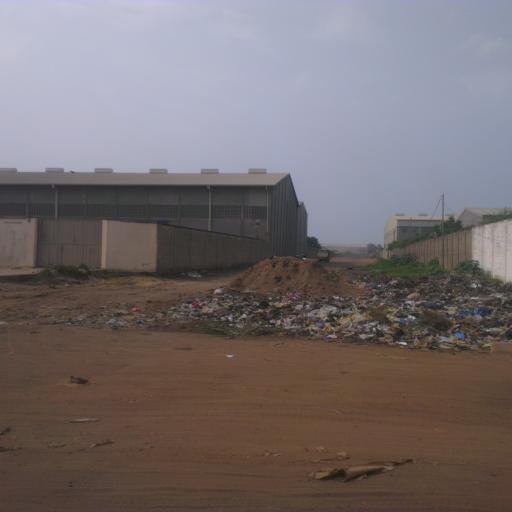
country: TG
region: Maritime
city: Lome
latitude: 6.1607
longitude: 1.2916
